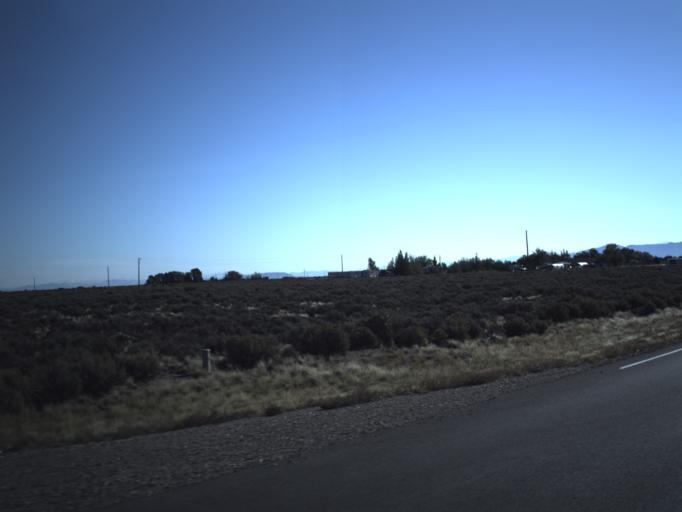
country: US
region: Utah
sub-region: Washington County
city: Enterprise
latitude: 37.7677
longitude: -113.8211
